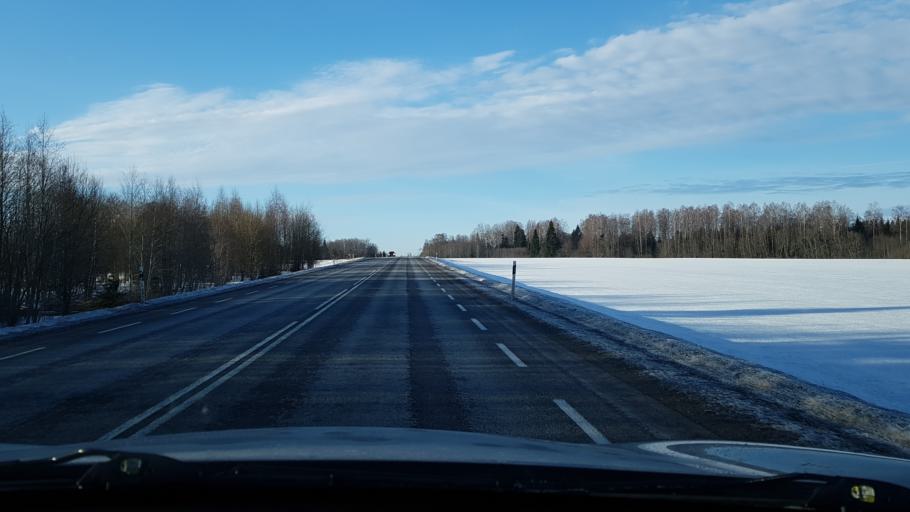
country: EE
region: Viljandimaa
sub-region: Vohma linn
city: Vohma
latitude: 58.6918
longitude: 25.7089
